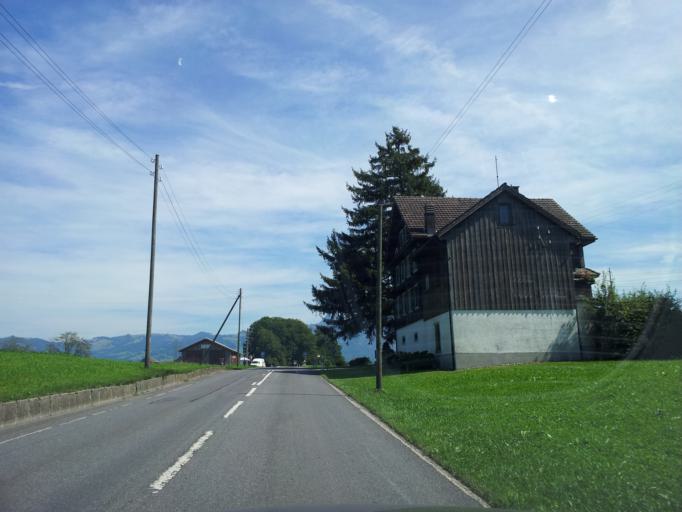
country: CH
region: Schwyz
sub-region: Bezirk March
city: Tuggen
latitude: 47.1918
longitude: 8.9319
